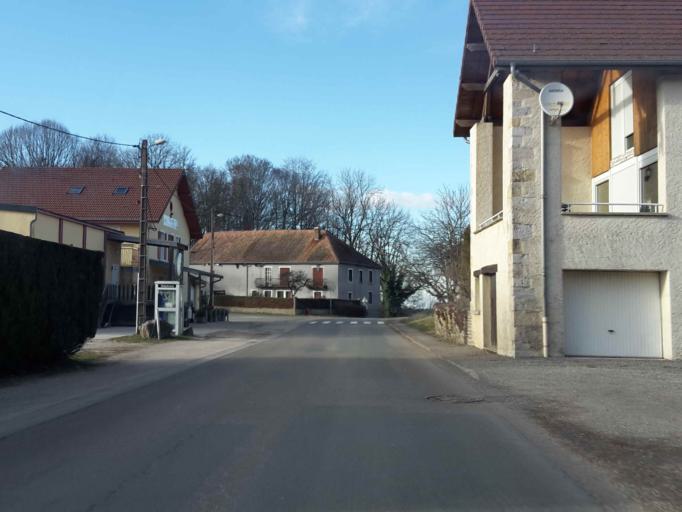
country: FR
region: Franche-Comte
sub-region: Departement du Doubs
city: Baume-les-Dames
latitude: 47.2748
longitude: 6.3827
